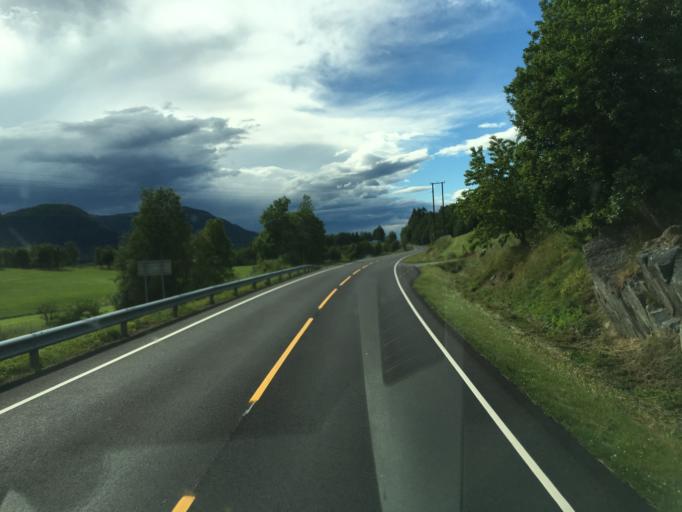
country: NO
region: More og Romsdal
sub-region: Tingvoll
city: Tingvoll
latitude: 62.9528
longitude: 8.1289
